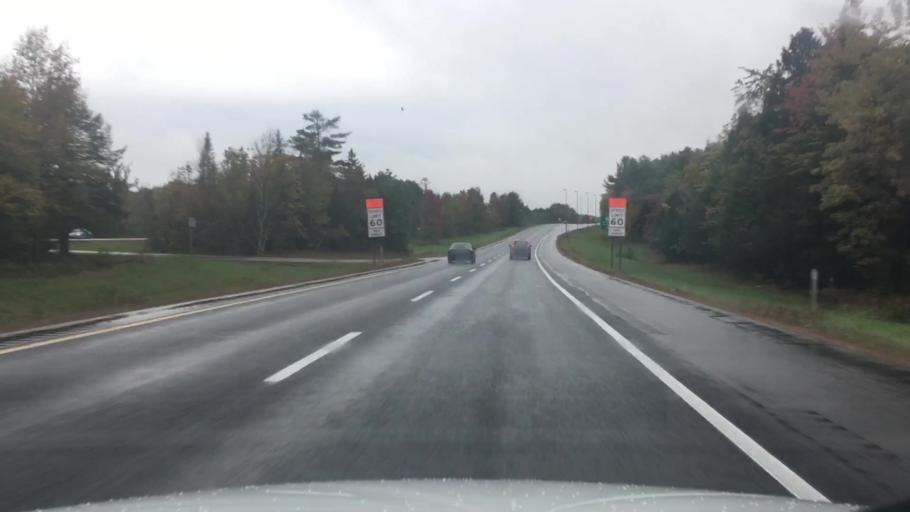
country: US
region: Maine
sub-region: Sagadahoc County
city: Richmond
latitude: 44.0920
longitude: -69.8739
